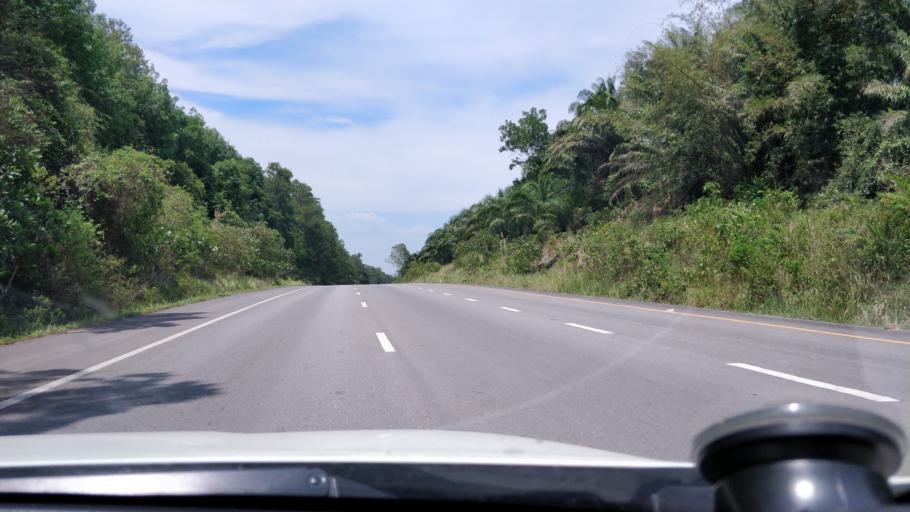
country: TH
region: Surat Thani
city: Chai Buri
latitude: 8.6367
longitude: 99.0184
